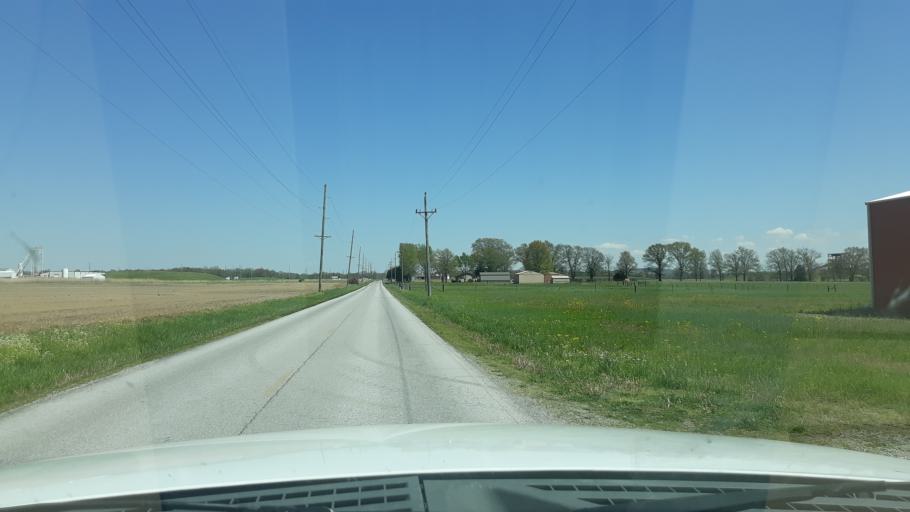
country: US
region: Illinois
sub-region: Saline County
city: Harrisburg
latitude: 37.8342
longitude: -88.6472
